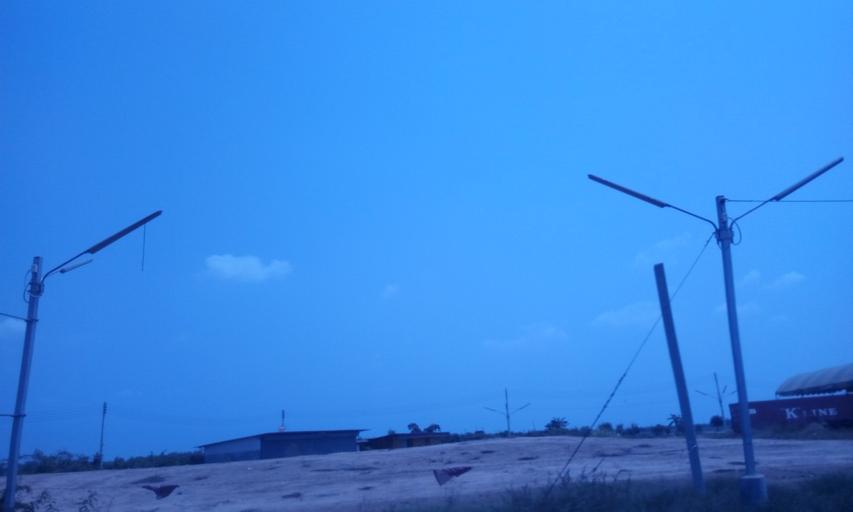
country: TH
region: Chachoengsao
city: Bang Nam Priao
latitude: 13.9634
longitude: 100.9668
